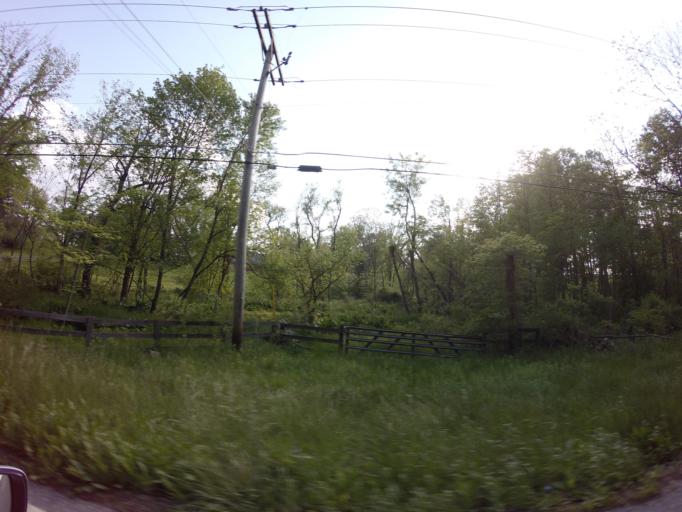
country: US
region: Maryland
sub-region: Baltimore County
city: Cockeysville
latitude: 39.5002
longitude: -76.7095
